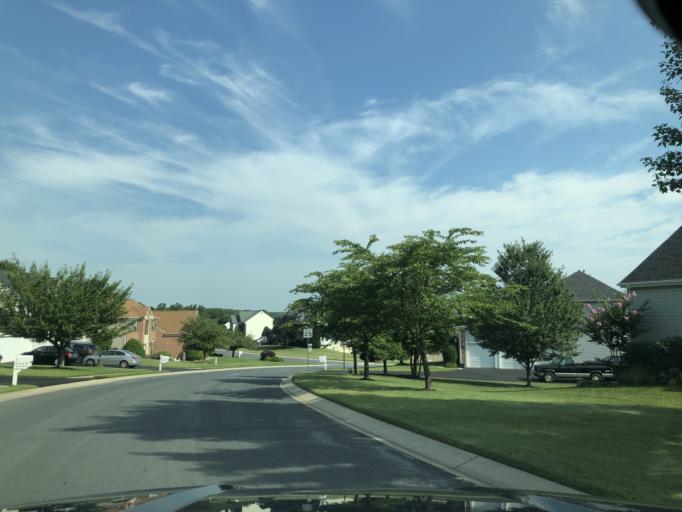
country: US
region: Maryland
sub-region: Carroll County
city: Eldersburg
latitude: 39.4121
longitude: -76.9663
